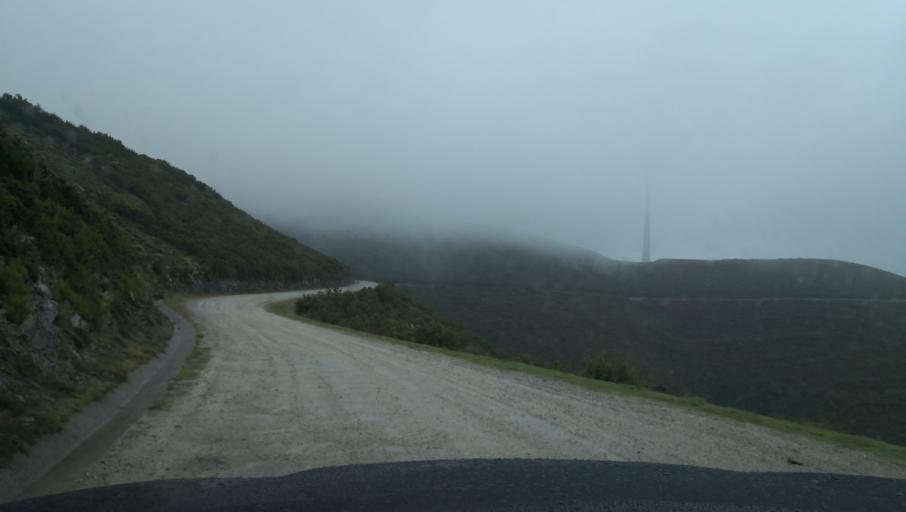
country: PT
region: Vila Real
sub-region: Vila Real
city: Vila Real
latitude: 41.3214
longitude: -7.8614
